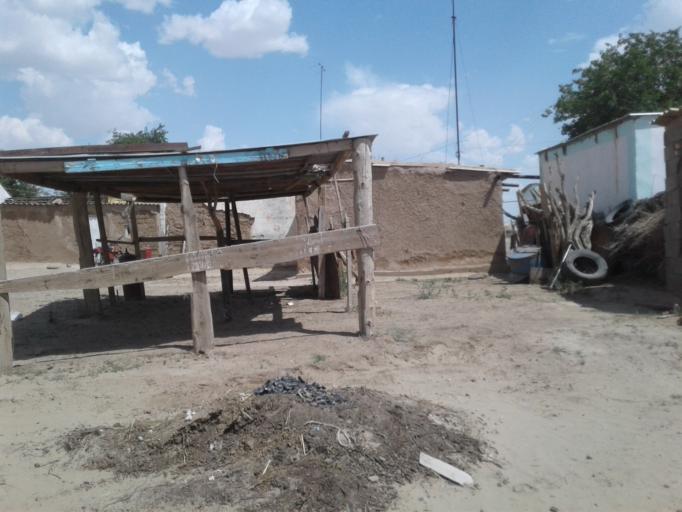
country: TM
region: Ahal
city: Abadan
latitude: 38.7658
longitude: 58.4936
